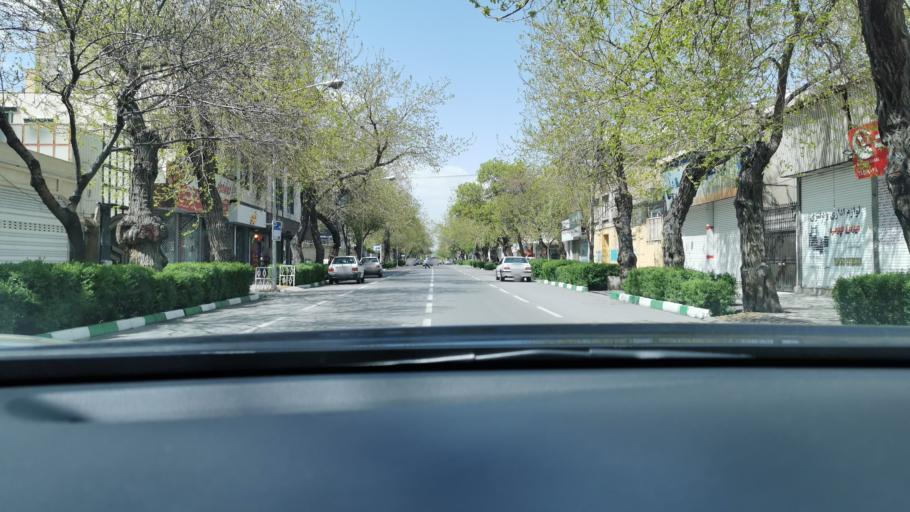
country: IR
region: Razavi Khorasan
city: Mashhad
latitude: 36.2974
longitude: 59.5945
